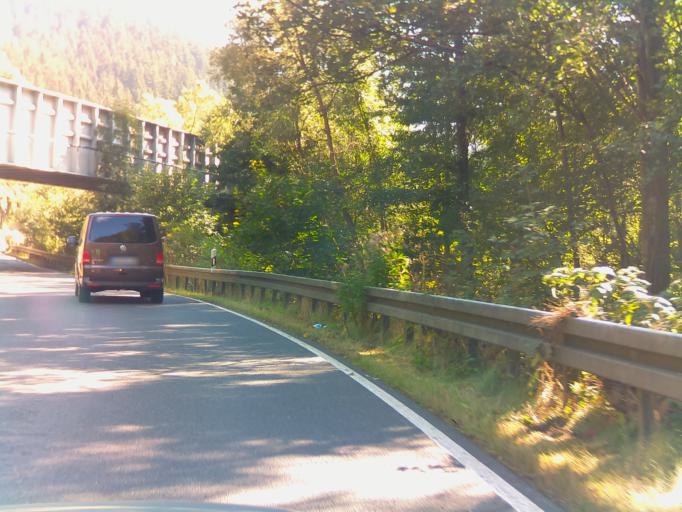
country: DE
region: Thuringia
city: Leutenberg
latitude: 50.5276
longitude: 11.4775
